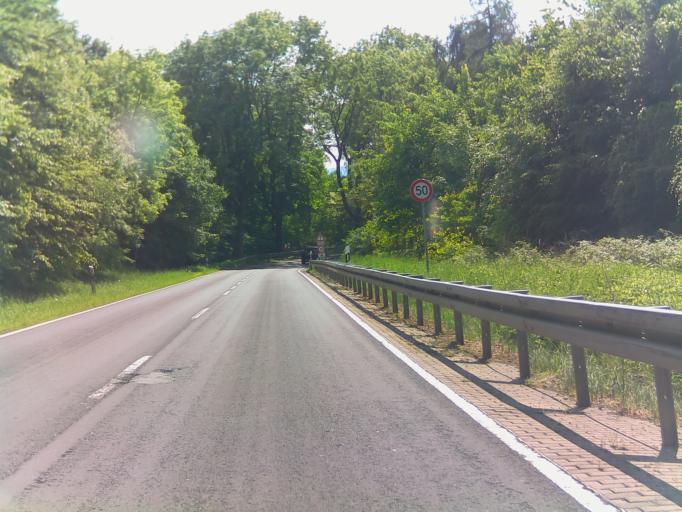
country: DE
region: Thuringia
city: Andenhausen
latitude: 50.6551
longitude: 10.0452
